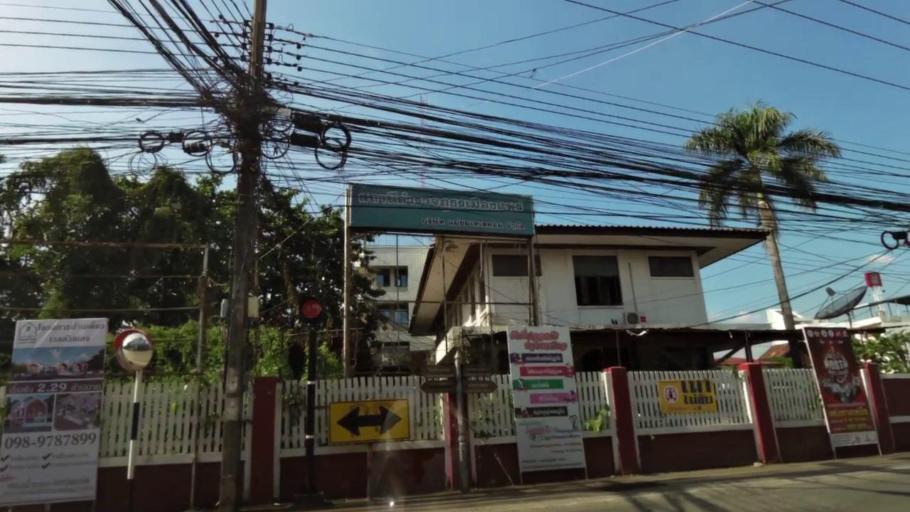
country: TH
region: Phrae
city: Phrae
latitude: 18.1411
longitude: 100.1421
